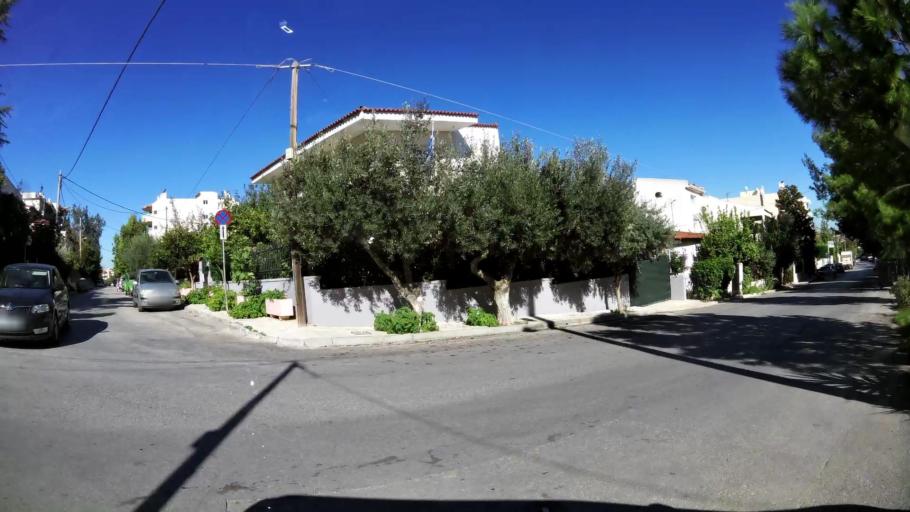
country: GR
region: Attica
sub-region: Nomarchia Anatolikis Attikis
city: Leondarion
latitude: 37.9844
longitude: 23.8479
